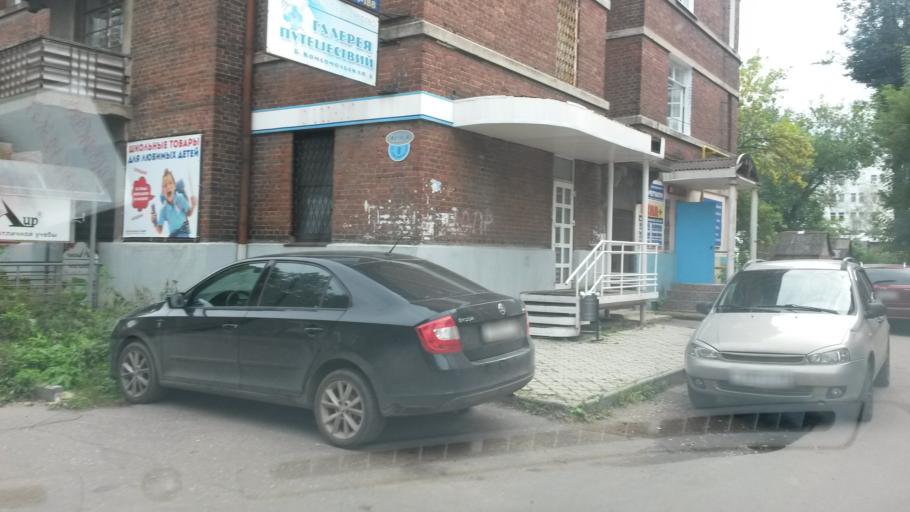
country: RU
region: Ivanovo
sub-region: Gorod Ivanovo
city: Ivanovo
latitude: 57.0078
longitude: 40.9733
